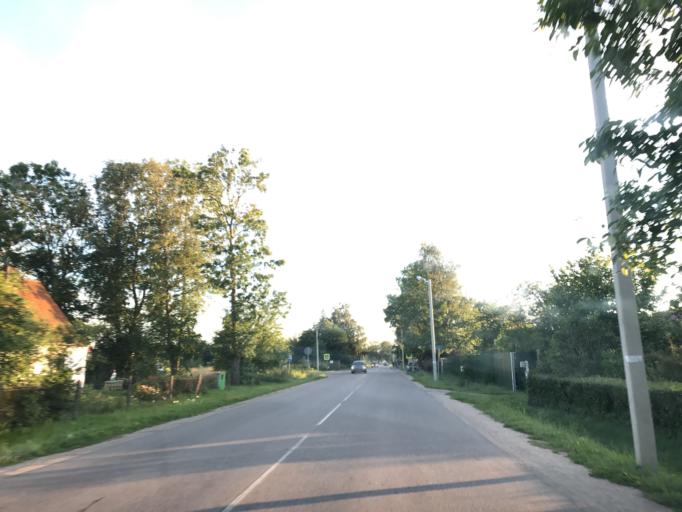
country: RU
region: Kaliningrad
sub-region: Zelenogradskiy Rayon
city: Zelenogradsk
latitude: 54.9393
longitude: 20.4522
